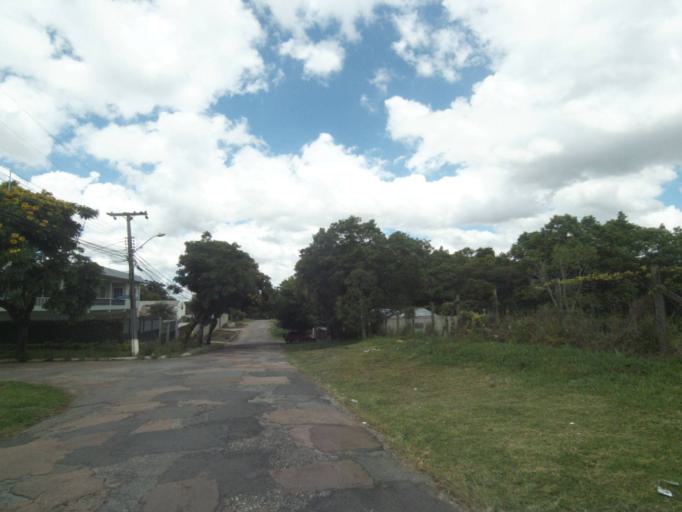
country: BR
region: Parana
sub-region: Curitiba
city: Curitiba
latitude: -25.4326
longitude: -49.3215
